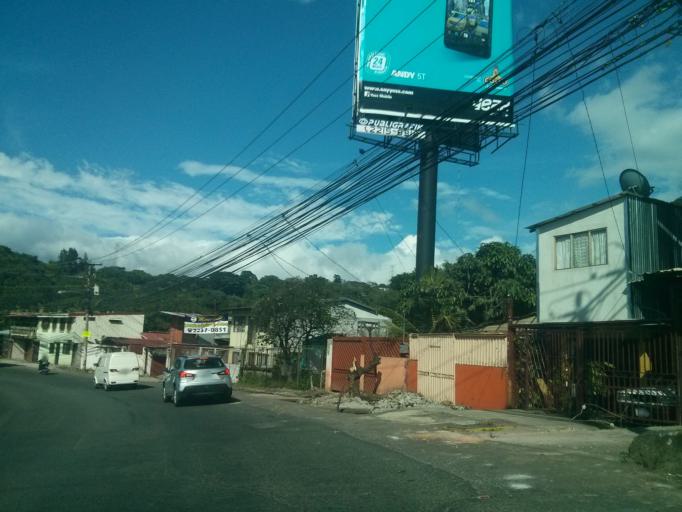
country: CR
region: San Jose
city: Colima
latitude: 9.9597
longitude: -84.1084
